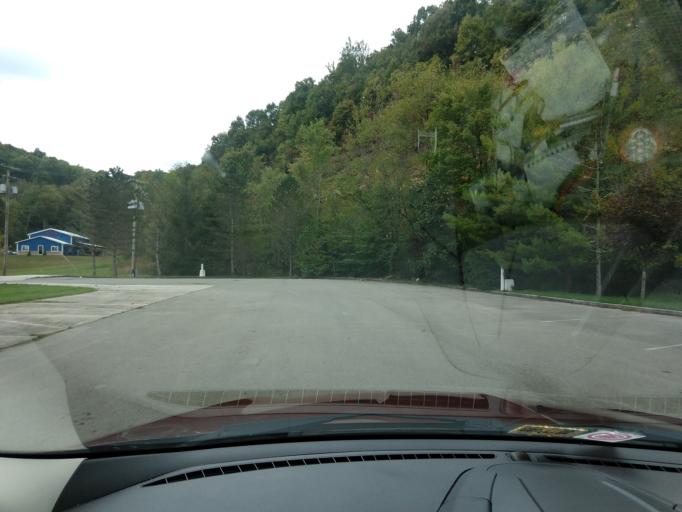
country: US
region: West Virginia
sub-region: Barbour County
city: Philippi
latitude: 39.1328
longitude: -80.0166
